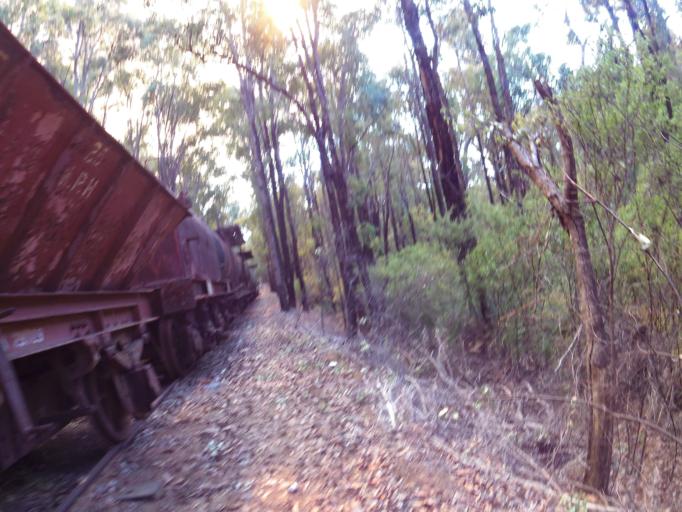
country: AU
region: Western Australia
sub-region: Waroona
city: Waroona
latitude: -32.7394
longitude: 116.1412
